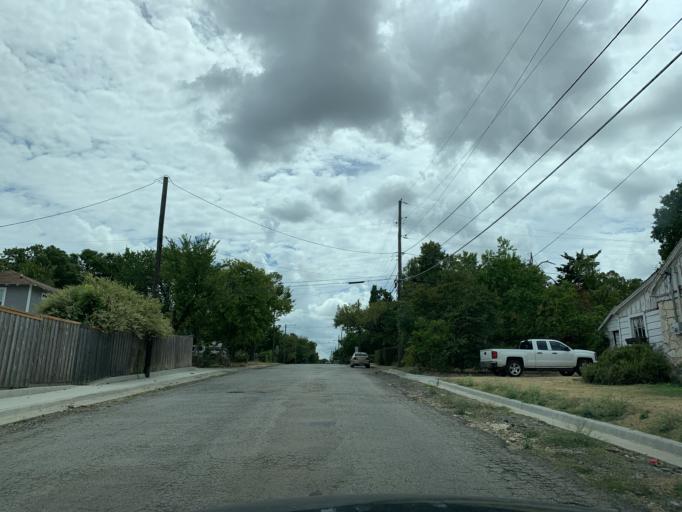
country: US
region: Texas
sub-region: Dallas County
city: Cockrell Hill
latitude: 32.7390
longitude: -96.8810
